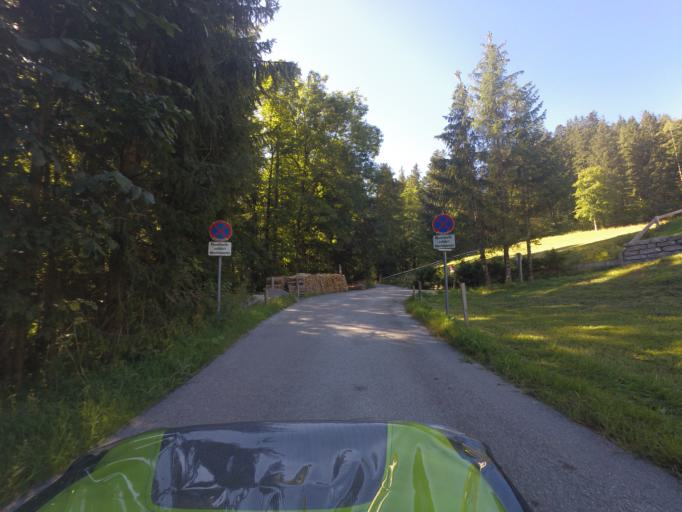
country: AT
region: Salzburg
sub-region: Politischer Bezirk Hallein
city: Hallein
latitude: 47.6529
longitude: 13.0970
